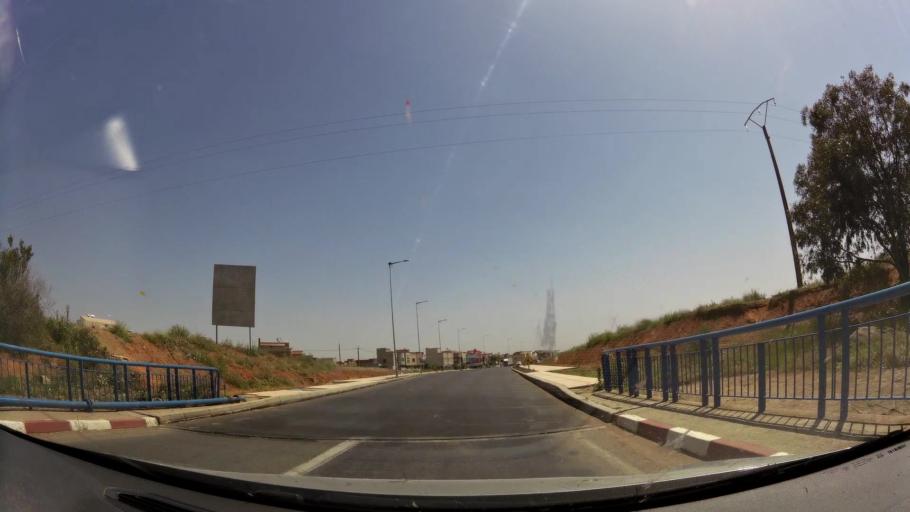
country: MA
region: Rabat-Sale-Zemmour-Zaer
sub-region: Khemisset
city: Khemisset
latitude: 33.8050
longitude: -6.0912
